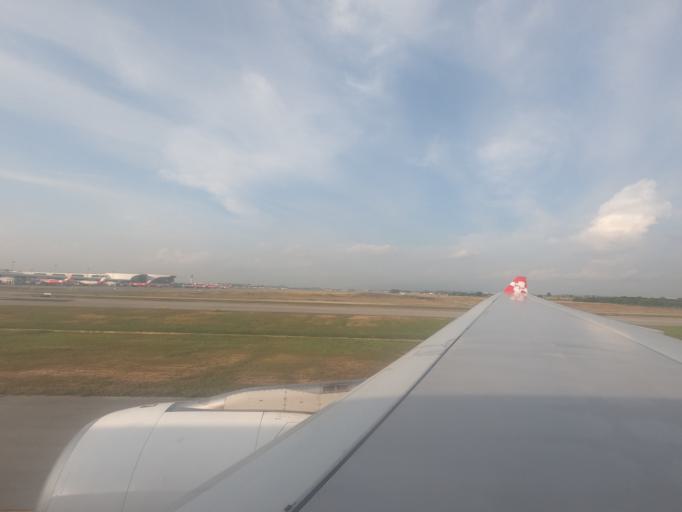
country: MY
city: Sungai Pelek New Village
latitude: 2.7314
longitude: 101.6842
